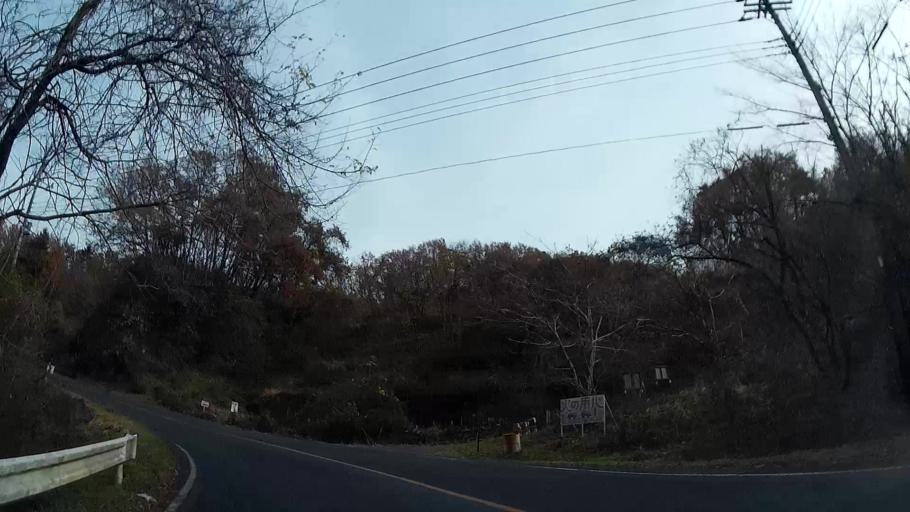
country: JP
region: Saitama
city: Chichibu
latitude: 35.9793
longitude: 139.0394
